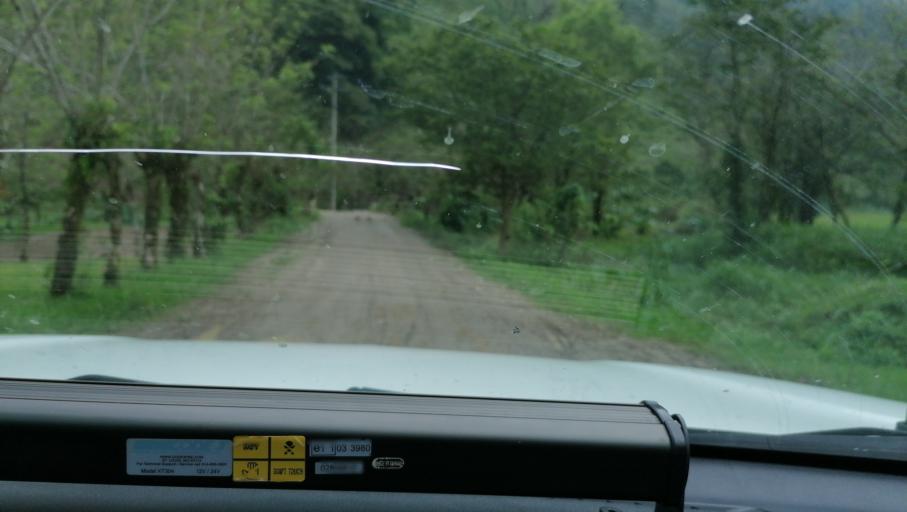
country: MX
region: Chiapas
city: Ixtacomitan
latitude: 17.3578
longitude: -93.1687
